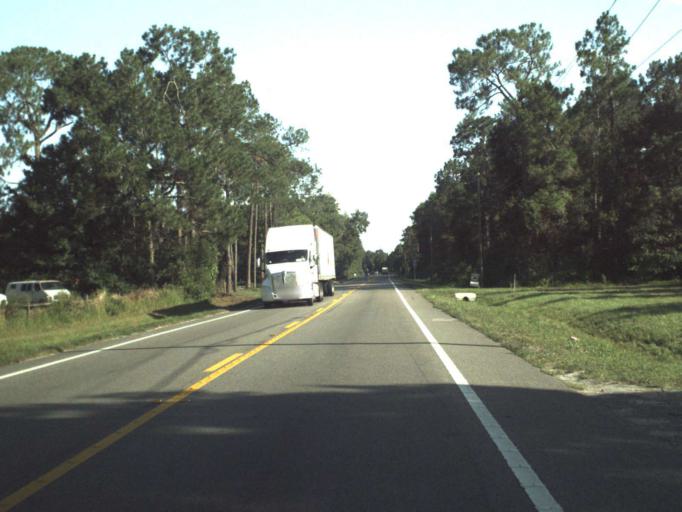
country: US
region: Florida
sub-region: Lake County
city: Clermont
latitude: 28.3806
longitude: -81.8240
